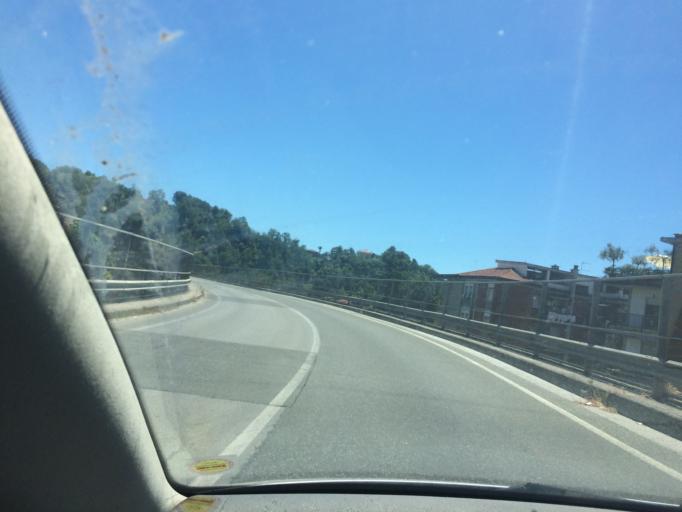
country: IT
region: Tuscany
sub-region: Provincia di Massa-Carrara
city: Carrara
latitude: 44.0711
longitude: 10.0848
